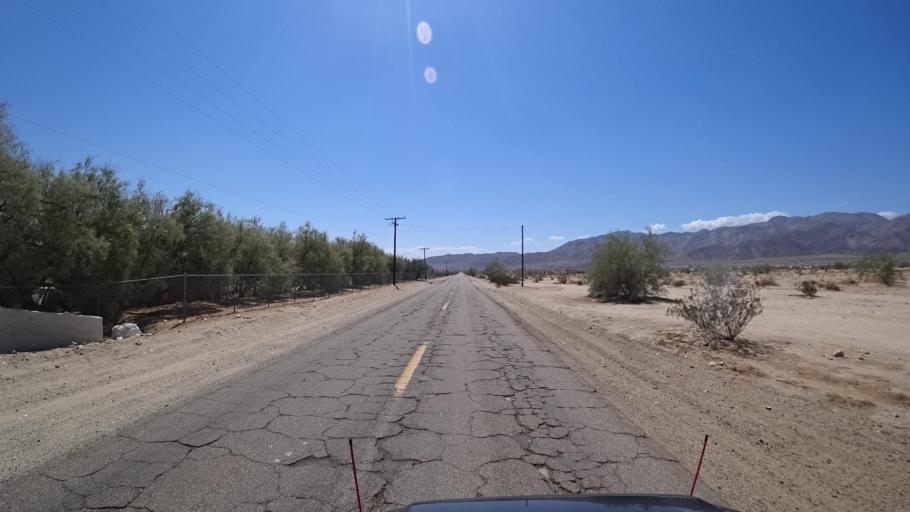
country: US
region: California
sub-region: Imperial County
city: Salton City
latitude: 33.1256
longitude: -116.1328
